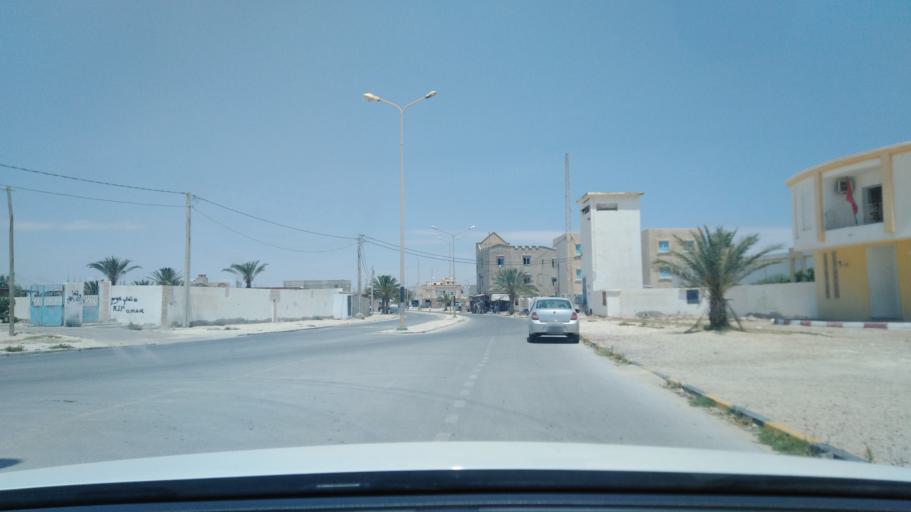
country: TN
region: Qabis
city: Gabes
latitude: 33.9493
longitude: 10.0696
